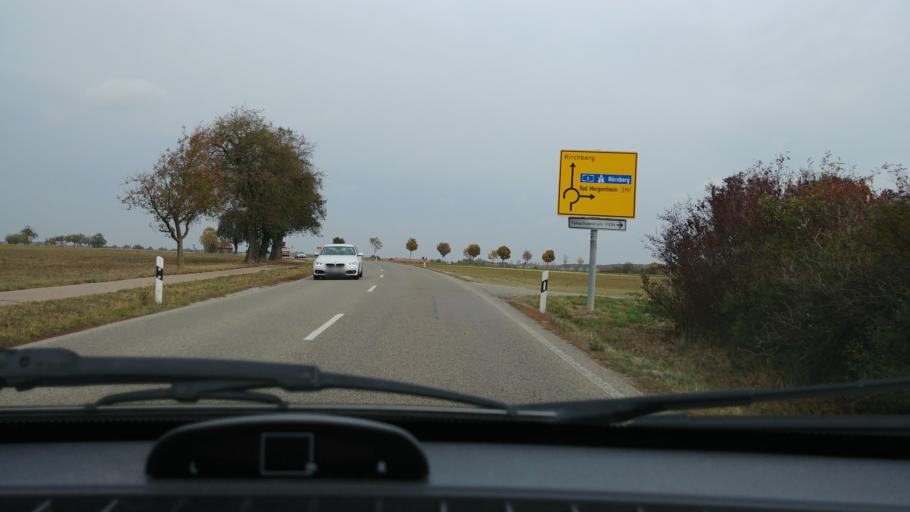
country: DE
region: Baden-Wuerttemberg
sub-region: Regierungsbezirk Stuttgart
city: Crailsheim
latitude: 49.1471
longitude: 10.0361
